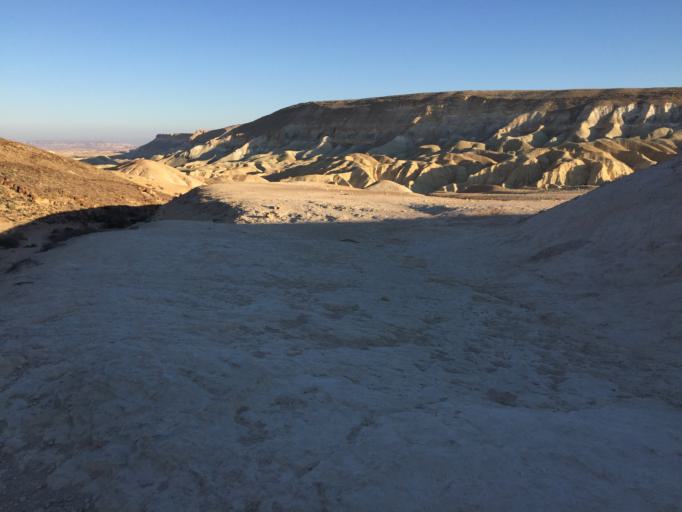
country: IL
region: Southern District
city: Midreshet Ben-Gurion
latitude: 30.8445
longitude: 34.7568
